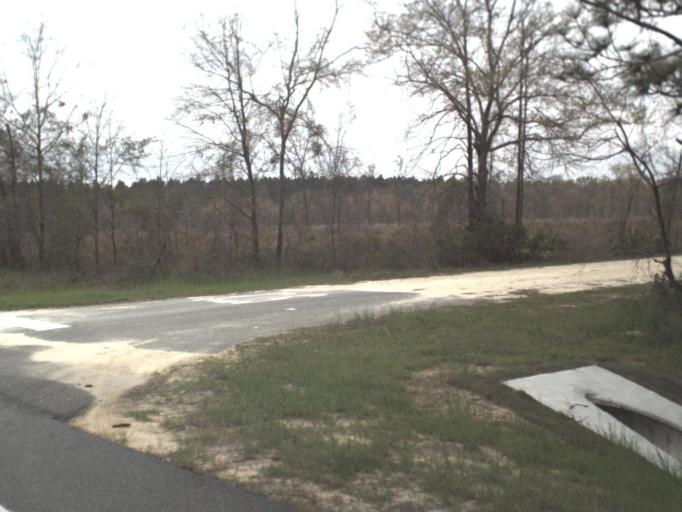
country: US
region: Florida
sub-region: Calhoun County
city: Blountstown
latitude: 30.3817
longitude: -85.2151
